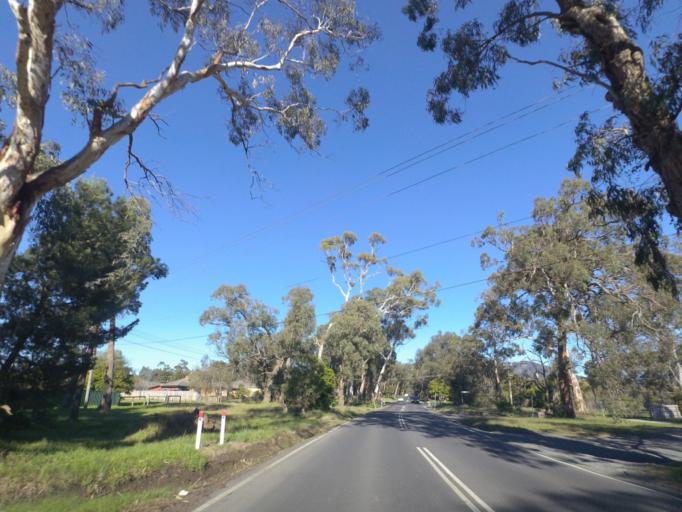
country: AU
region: Victoria
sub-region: Yarra Ranges
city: Kilsyth
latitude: -37.7954
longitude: 145.3234
